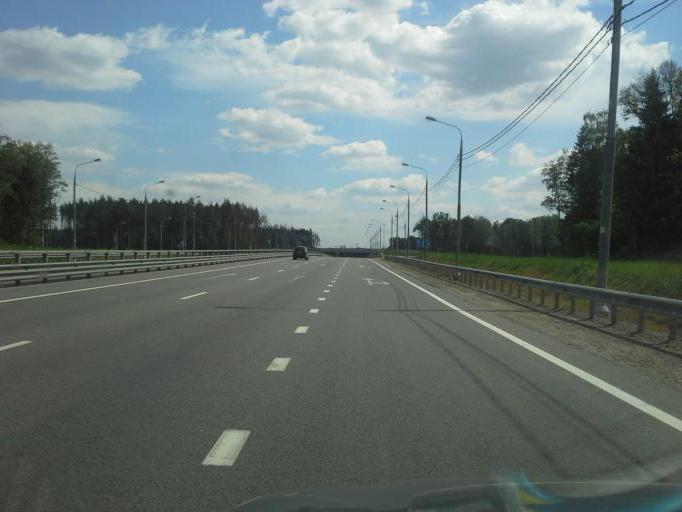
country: RU
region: Moskovskaya
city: Odintsovo
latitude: 55.6976
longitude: 37.2688
